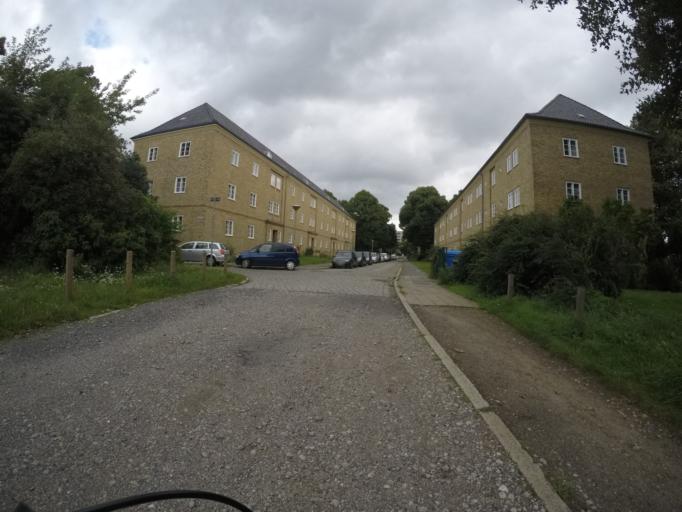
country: DE
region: Brandenburg
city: Potsdam
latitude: 52.3906
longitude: 13.0363
